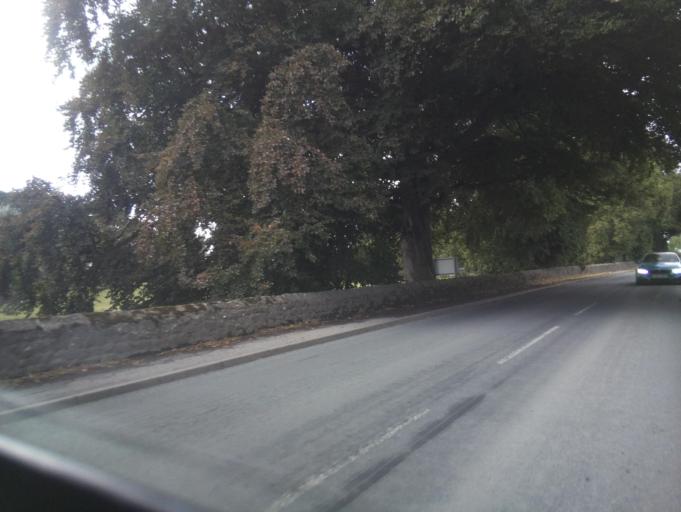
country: GB
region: England
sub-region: North Yorkshire
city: Bedale
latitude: 54.2243
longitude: -1.6614
